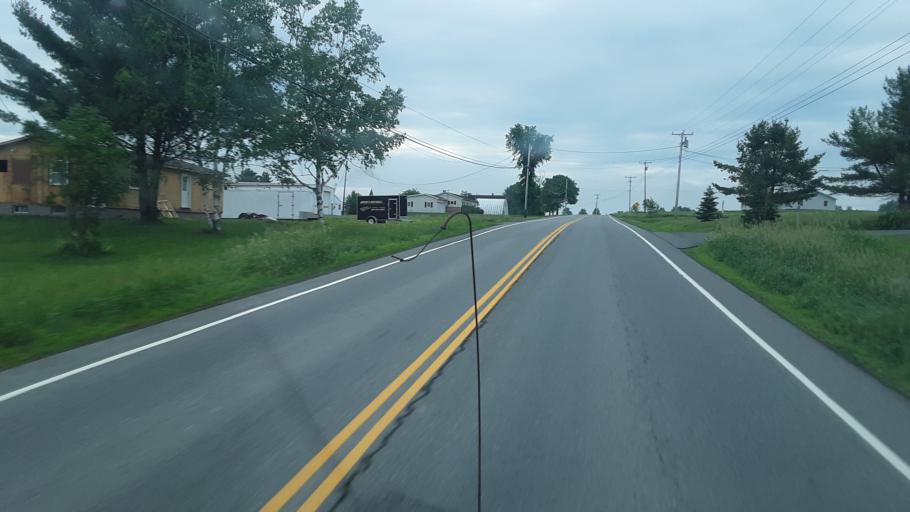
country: US
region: Maine
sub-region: Aroostook County
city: Presque Isle
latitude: 46.6207
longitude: -68.4010
